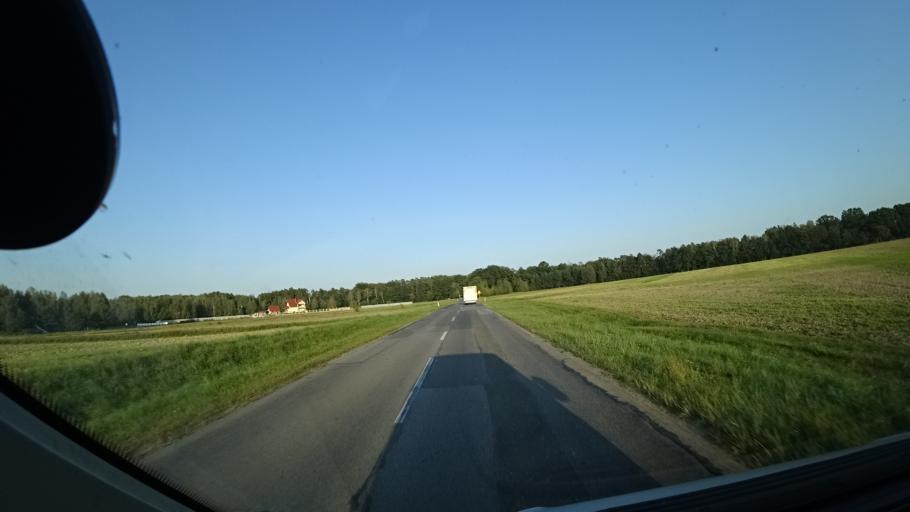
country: PL
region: Silesian Voivodeship
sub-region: Powiat gliwicki
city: Sosnicowice
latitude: 50.2794
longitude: 18.4819
